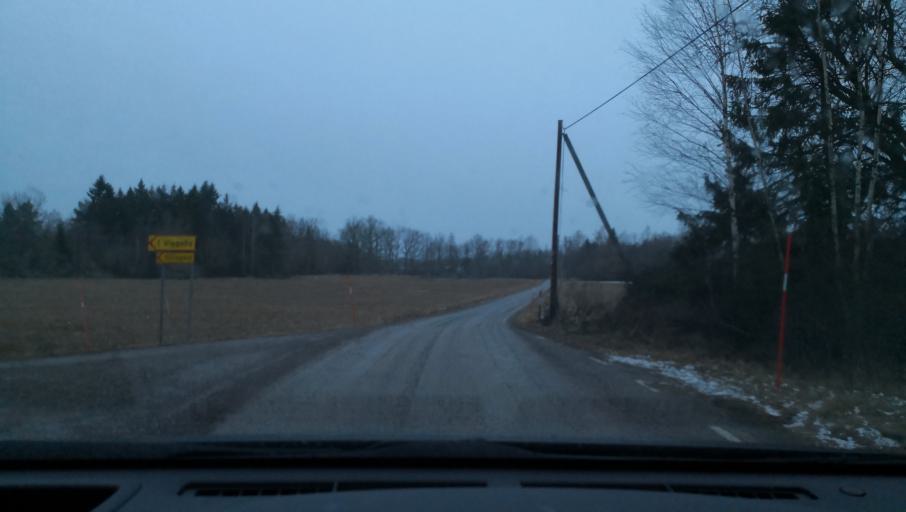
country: SE
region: Uppsala
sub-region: Enkopings Kommun
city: Hummelsta
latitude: 59.4567
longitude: 16.8258
